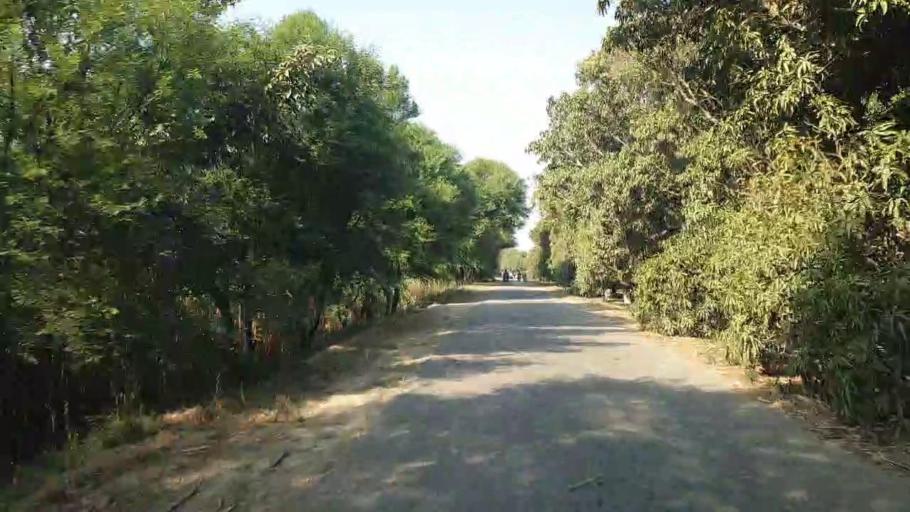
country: PK
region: Sindh
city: Mirwah Gorchani
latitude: 25.3775
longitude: 68.9511
